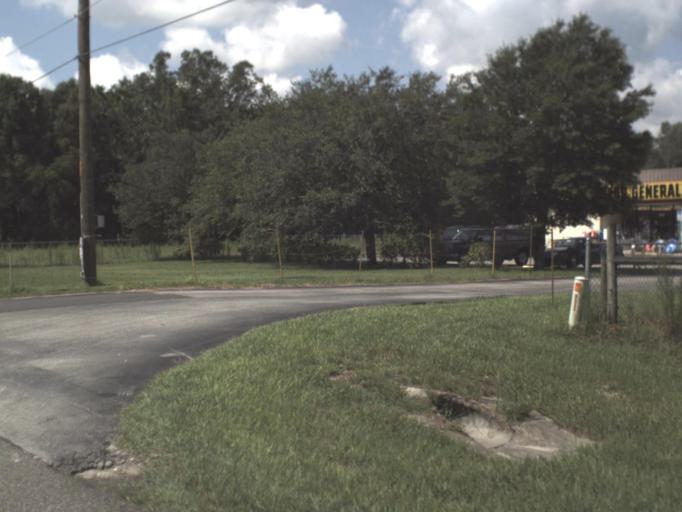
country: US
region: Florida
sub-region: Citrus County
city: Floral City
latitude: 28.7624
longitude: -82.2937
